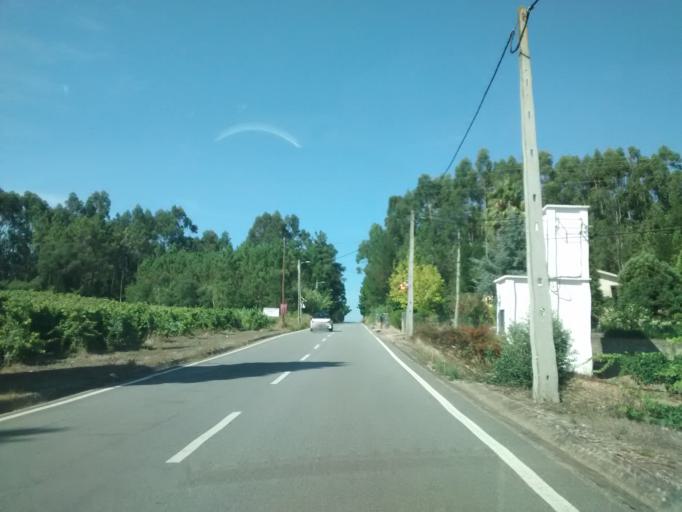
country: PT
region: Aveiro
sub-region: Anadia
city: Sangalhos
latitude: 40.4369
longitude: -8.5021
